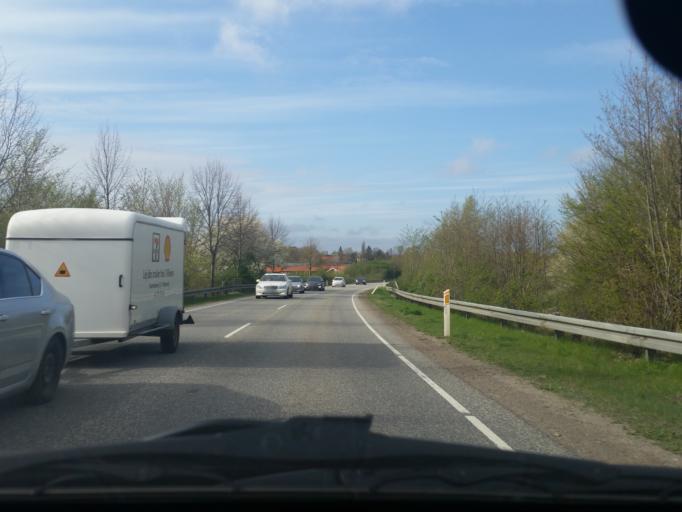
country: DK
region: Zealand
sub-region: Soro Kommune
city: Soro
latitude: 55.4480
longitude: 11.5623
